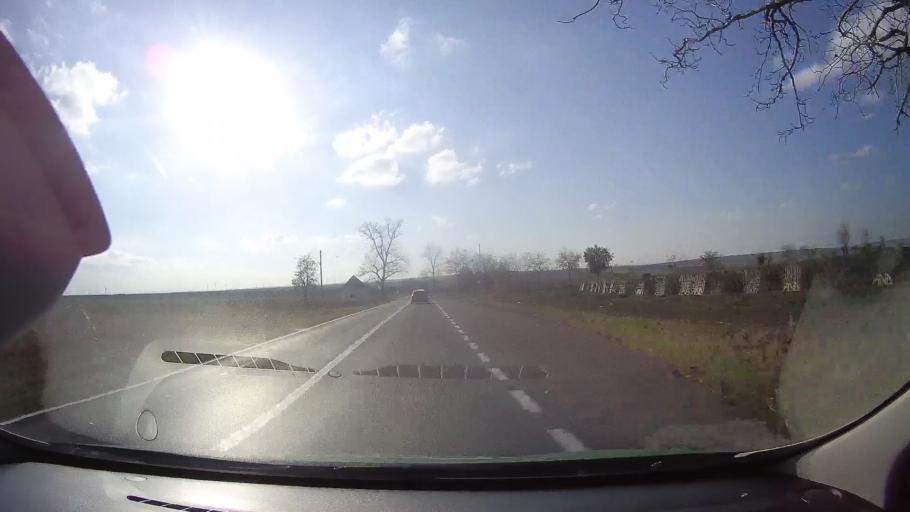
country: RO
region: Tulcea
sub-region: Comuna Topolog
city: Topolog
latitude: 44.8480
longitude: 28.3193
